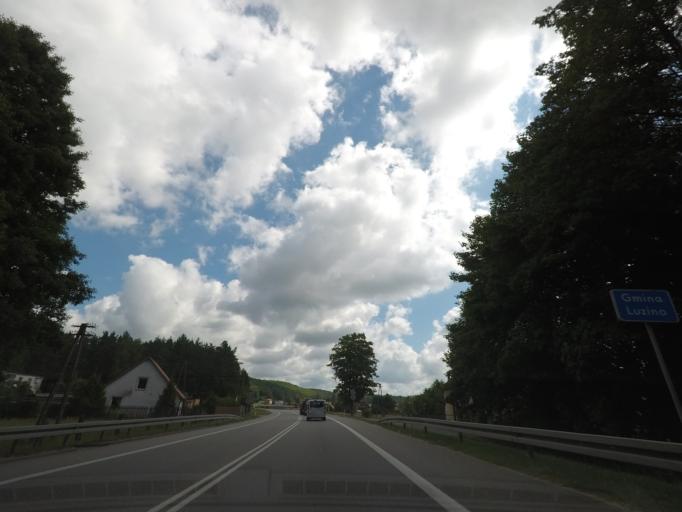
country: PL
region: Pomeranian Voivodeship
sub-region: Powiat wejherowski
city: Luzino
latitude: 54.5687
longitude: 18.0529
